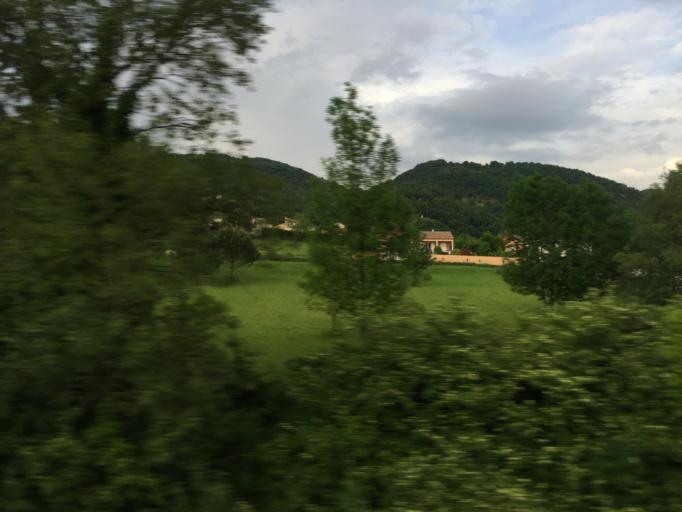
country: FR
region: Rhone-Alpes
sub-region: Departement de la Drome
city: Saint-Vallier
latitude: 45.1597
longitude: 4.8322
